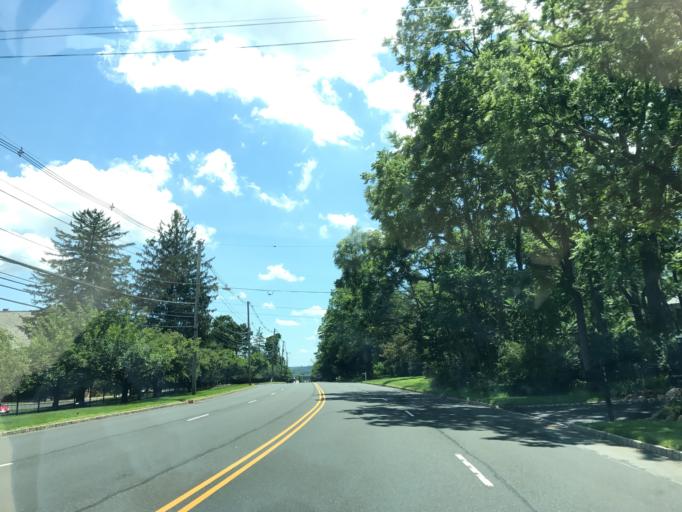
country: US
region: New Jersey
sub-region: Morris County
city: Madison
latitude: 40.7884
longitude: -74.4336
